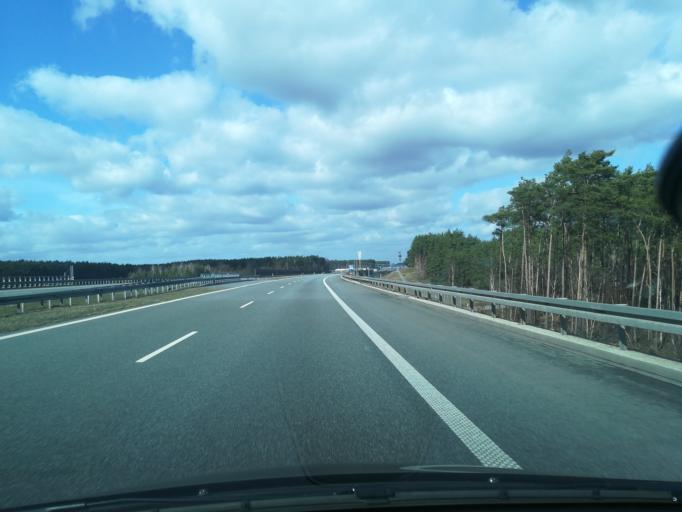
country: PL
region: Kujawsko-Pomorskie
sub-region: Powiat aleksandrowski
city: Aleksandrow Kujawski
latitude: 52.8926
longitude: 18.7279
